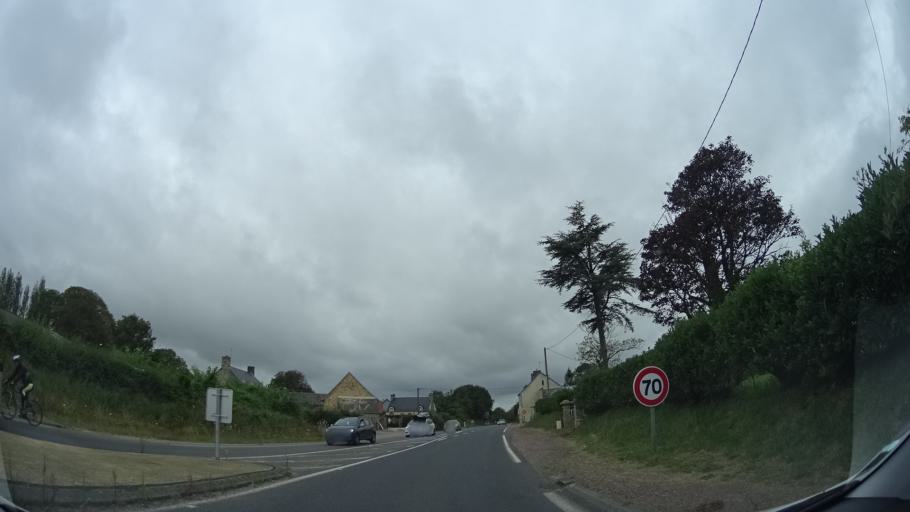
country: FR
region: Lower Normandy
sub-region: Departement de la Manche
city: La Haye-du-Puits
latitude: 49.2954
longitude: -1.5587
